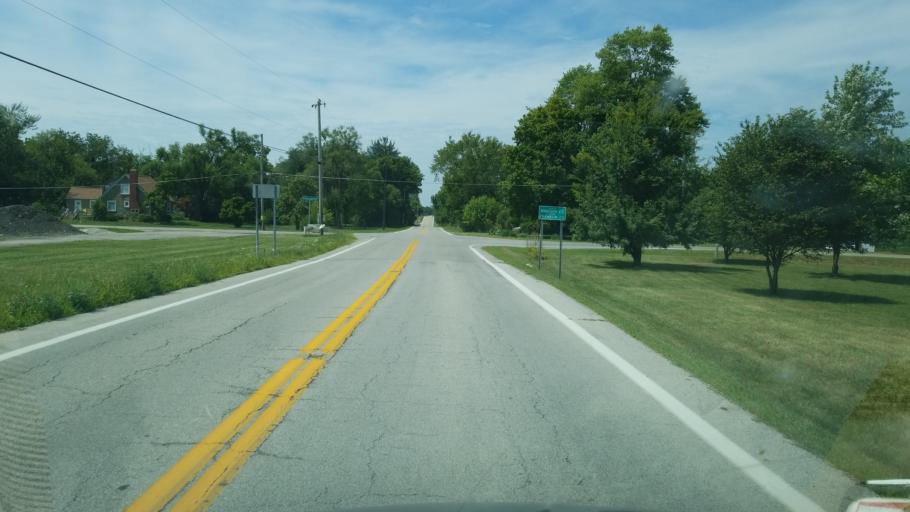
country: US
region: Ohio
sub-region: Madison County
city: West Jefferson
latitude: 39.8607
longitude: -83.2471
